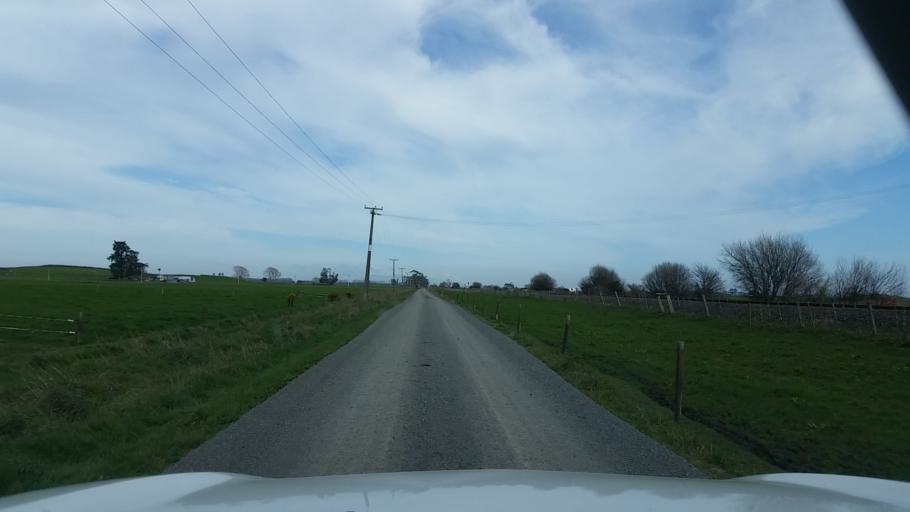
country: NZ
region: Waikato
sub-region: Waipa District
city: Cambridge
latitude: -37.6782
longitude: 175.4606
